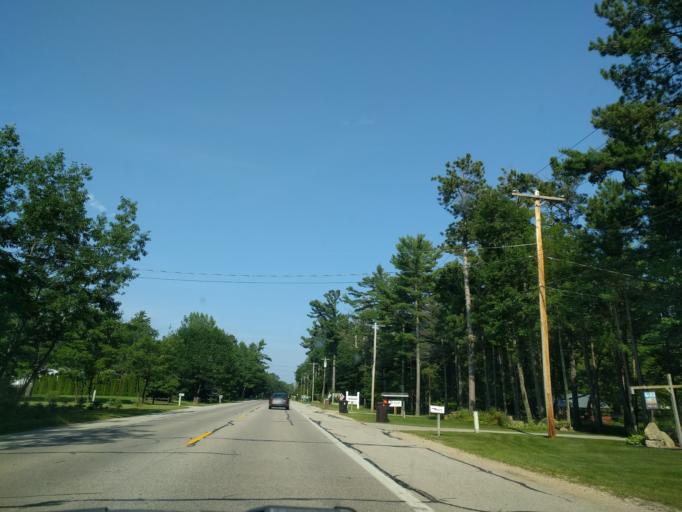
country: US
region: Michigan
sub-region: Delta County
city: Escanaba
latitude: 45.6824
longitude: -87.1316
